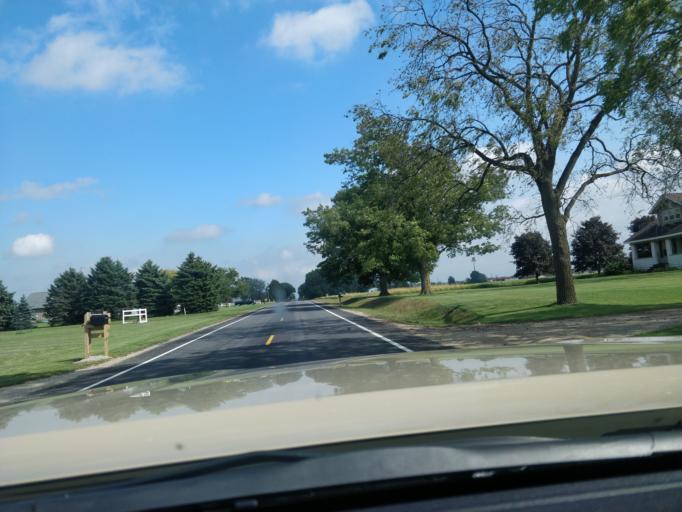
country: US
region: Michigan
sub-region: Ionia County
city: Ionia
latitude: 42.8861
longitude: -85.0836
